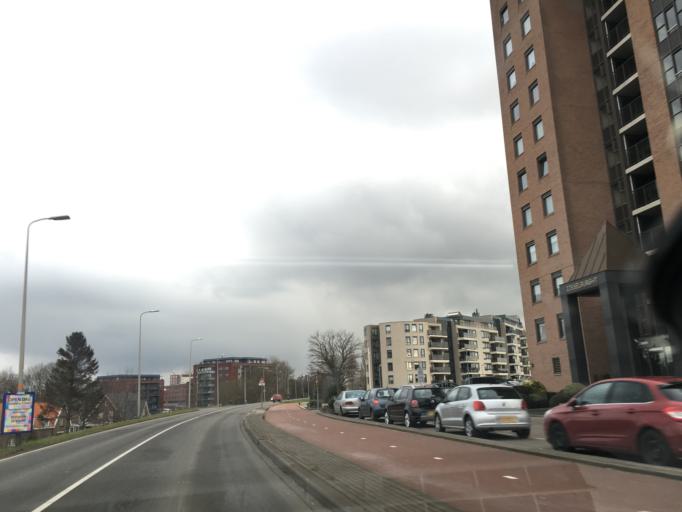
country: NL
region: South Holland
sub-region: Gemeente Capelle aan den IJssel
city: Capelle aan den IJssel
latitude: 51.9196
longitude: 4.5781
